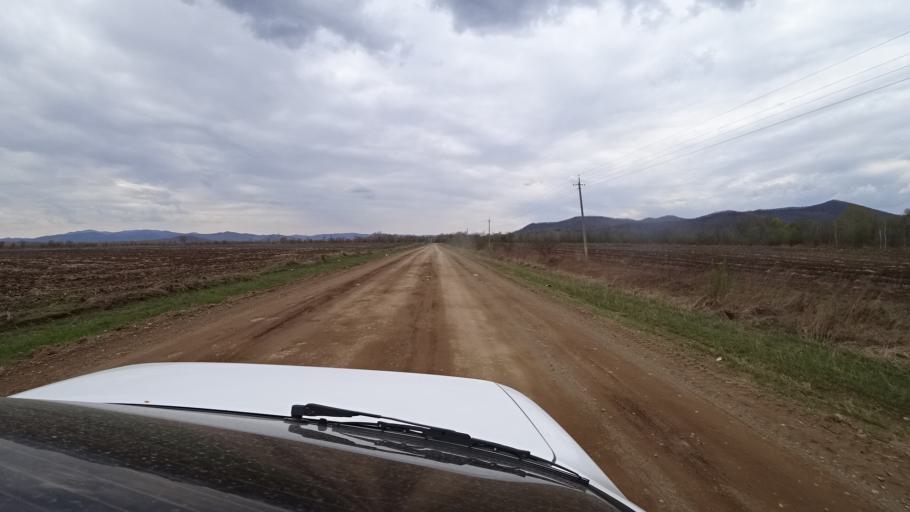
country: RU
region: Primorskiy
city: Novopokrovka
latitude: 45.5564
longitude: 134.3557
